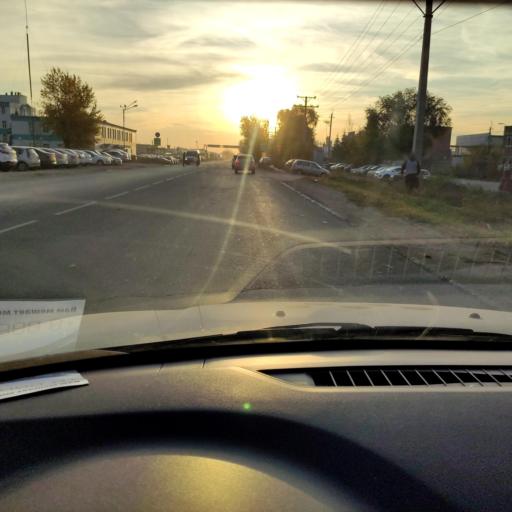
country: RU
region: Samara
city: Tol'yatti
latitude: 53.5338
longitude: 49.4457
